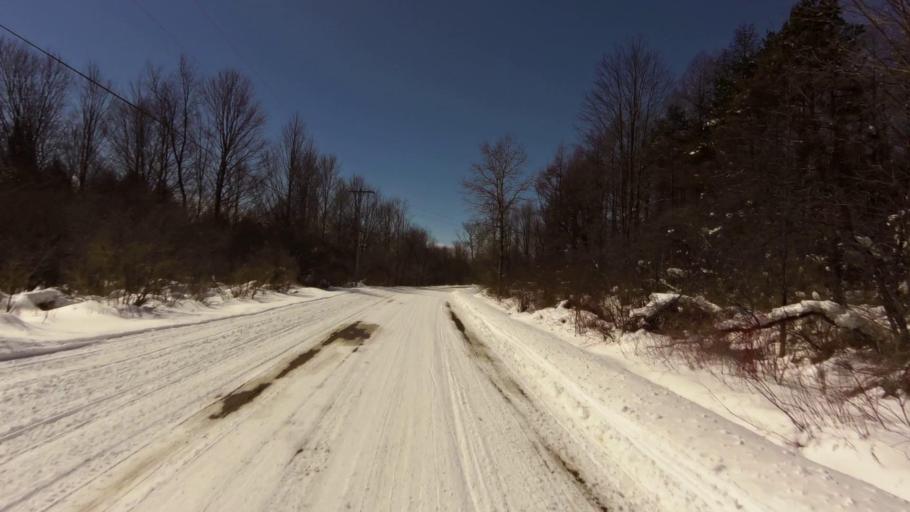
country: US
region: New York
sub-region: Wyoming County
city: Arcade
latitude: 42.4414
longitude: -78.3311
